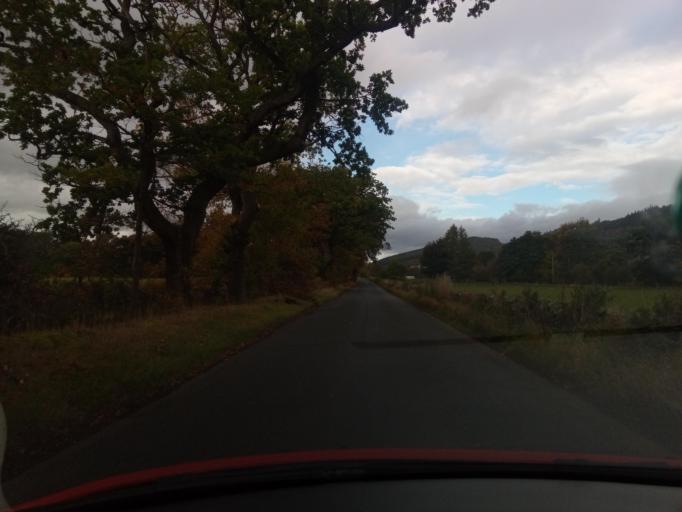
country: GB
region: Scotland
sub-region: The Scottish Borders
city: Peebles
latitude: 55.6410
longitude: -3.1593
